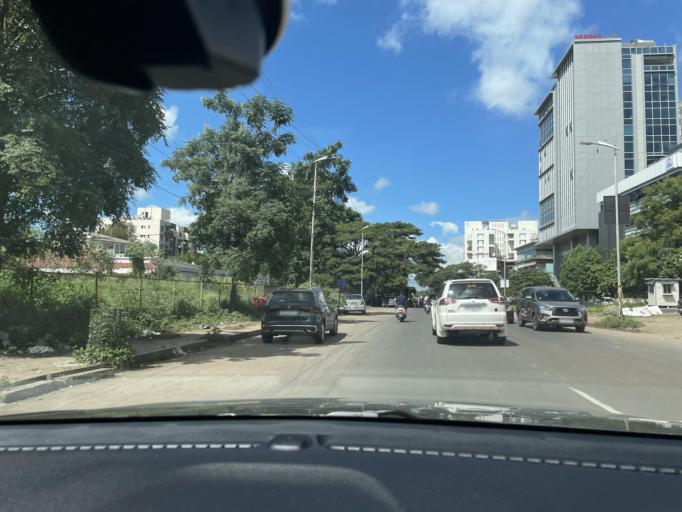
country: IN
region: Maharashtra
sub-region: Pune Division
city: Shivaji Nagar
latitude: 18.5215
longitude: 73.7794
